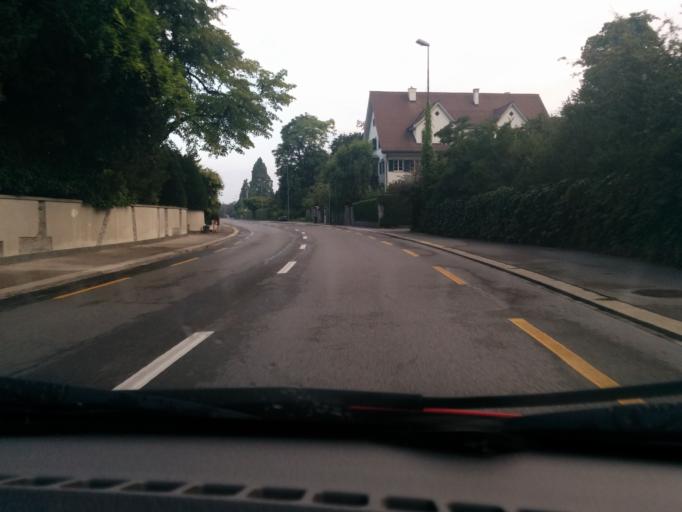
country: CH
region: Zurich
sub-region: Bezirk Meilen
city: Kuesnacht / Goldbach
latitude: 47.3295
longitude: 8.5732
